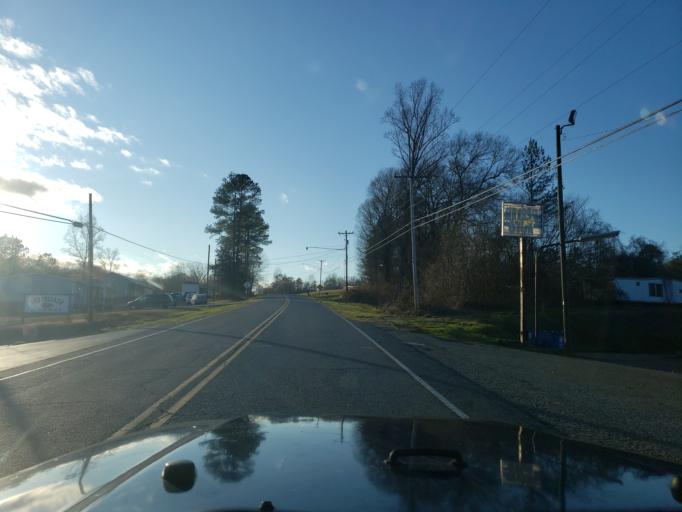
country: US
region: North Carolina
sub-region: Cleveland County
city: Shelby
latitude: 35.4152
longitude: -81.5723
